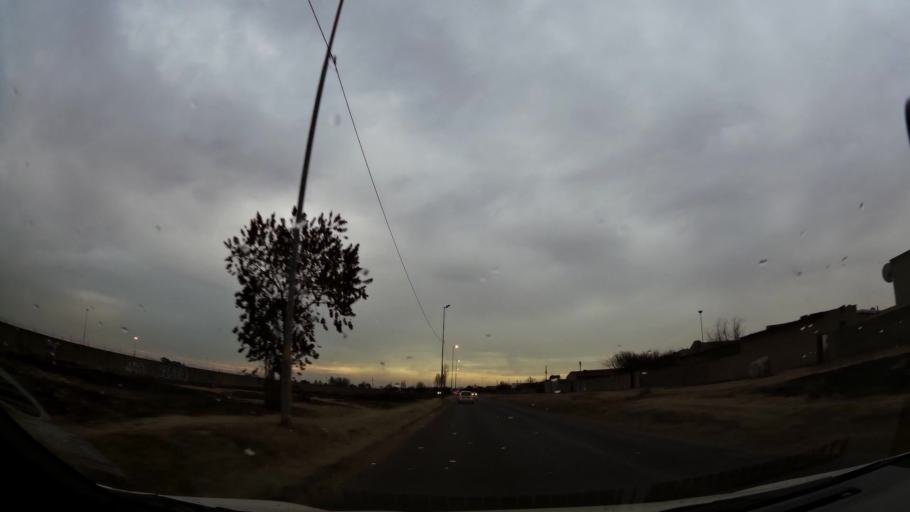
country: ZA
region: Gauteng
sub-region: Ekurhuleni Metropolitan Municipality
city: Germiston
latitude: -26.3616
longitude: 28.1846
